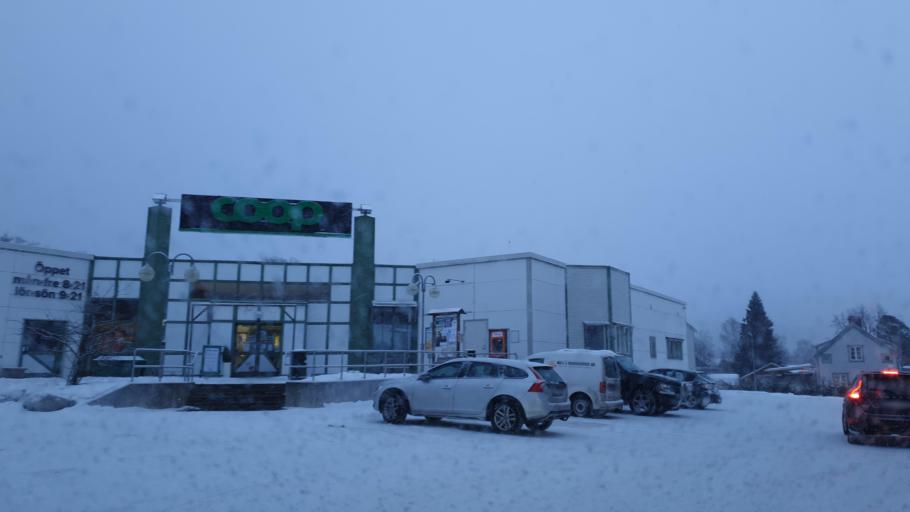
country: SE
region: Vaesternorrland
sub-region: OErnskoeldsviks Kommun
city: Ornskoldsvik
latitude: 63.2941
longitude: 18.6227
